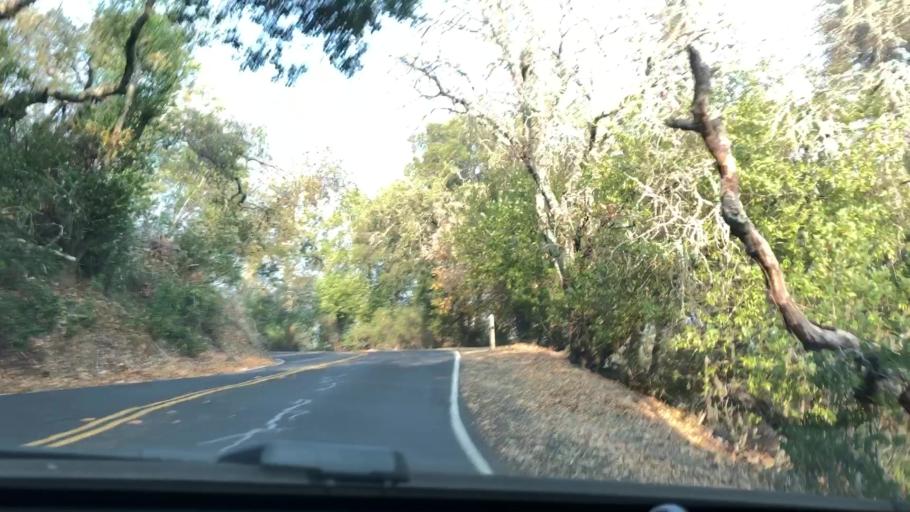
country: US
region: California
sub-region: Contra Costa County
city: Orinda
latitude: 37.8999
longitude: -122.2135
